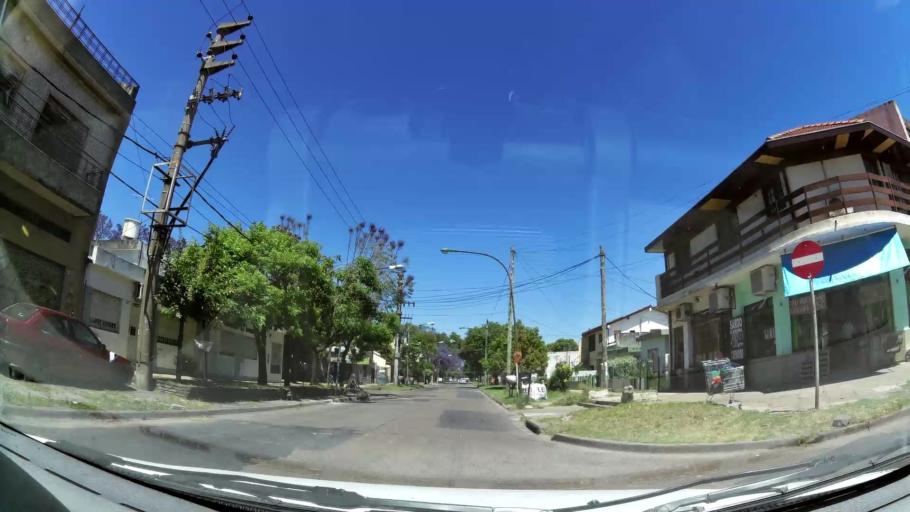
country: AR
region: Buenos Aires
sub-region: Partido de Vicente Lopez
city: Olivos
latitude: -34.5158
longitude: -58.5333
